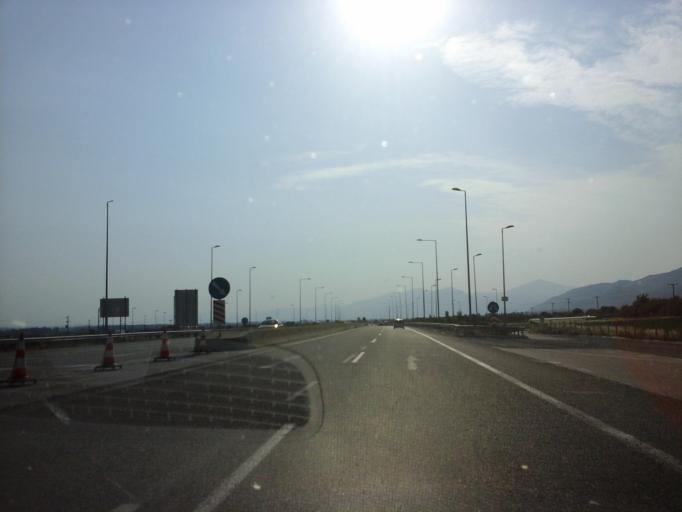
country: GR
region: East Macedonia and Thrace
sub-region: Nomos Xanthis
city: Selero
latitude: 41.1205
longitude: 25.0798
